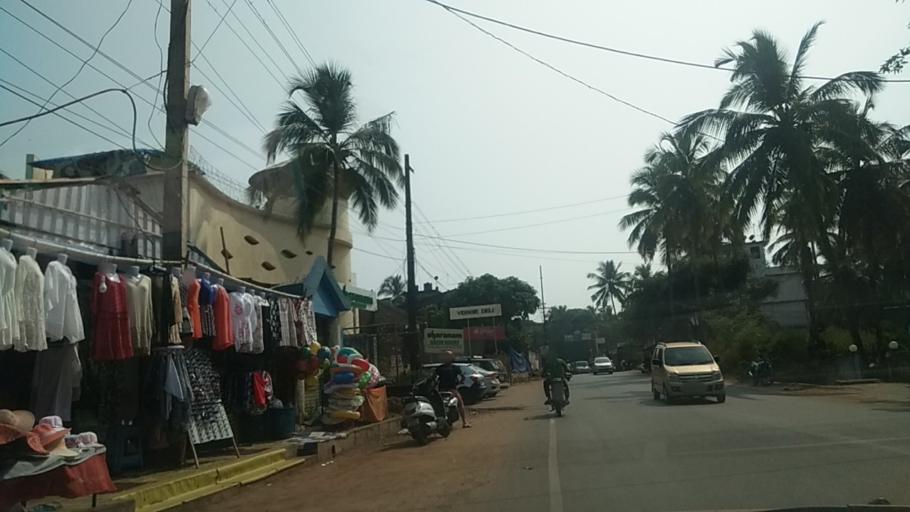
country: IN
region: Goa
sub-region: North Goa
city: Candolim
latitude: 15.5322
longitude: 73.7644
